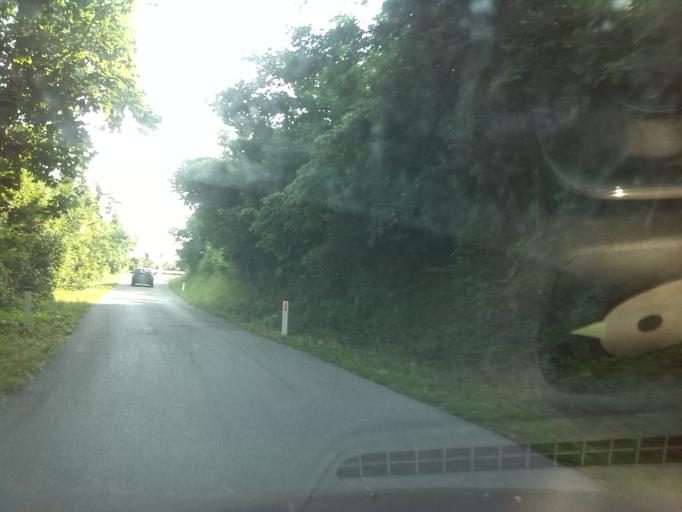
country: IT
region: Friuli Venezia Giulia
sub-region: Provincia di Udine
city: Cras
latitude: 46.1805
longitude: 13.6675
